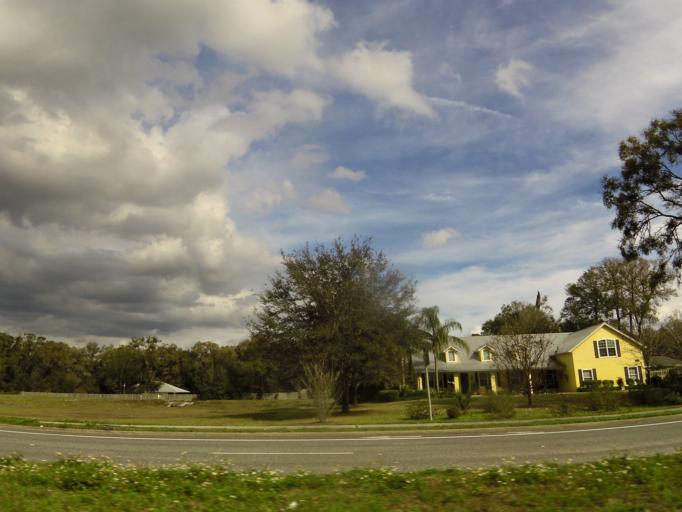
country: US
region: Florida
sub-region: Volusia County
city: North DeLand
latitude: 29.0682
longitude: -81.3253
